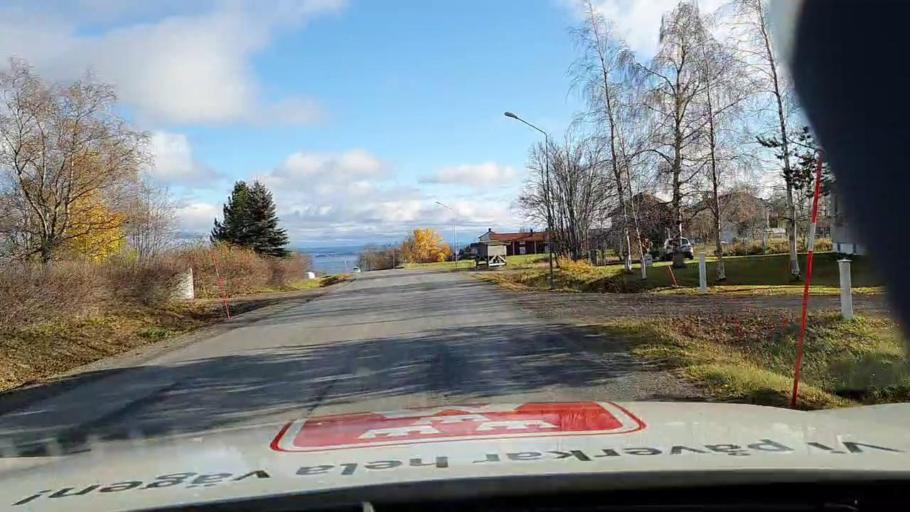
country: SE
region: Jaemtland
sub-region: Krokoms Kommun
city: Krokom
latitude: 63.1830
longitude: 14.0596
